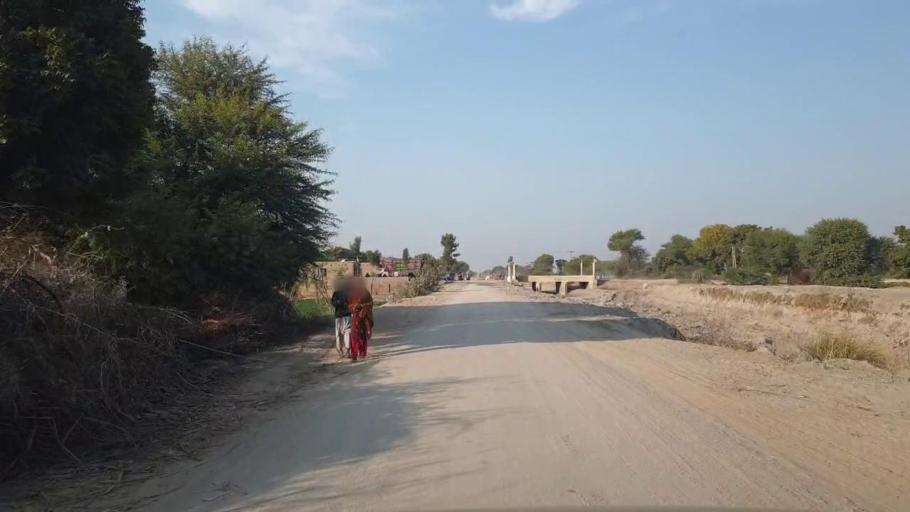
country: PK
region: Sindh
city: Shahpur Chakar
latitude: 26.1567
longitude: 68.6407
